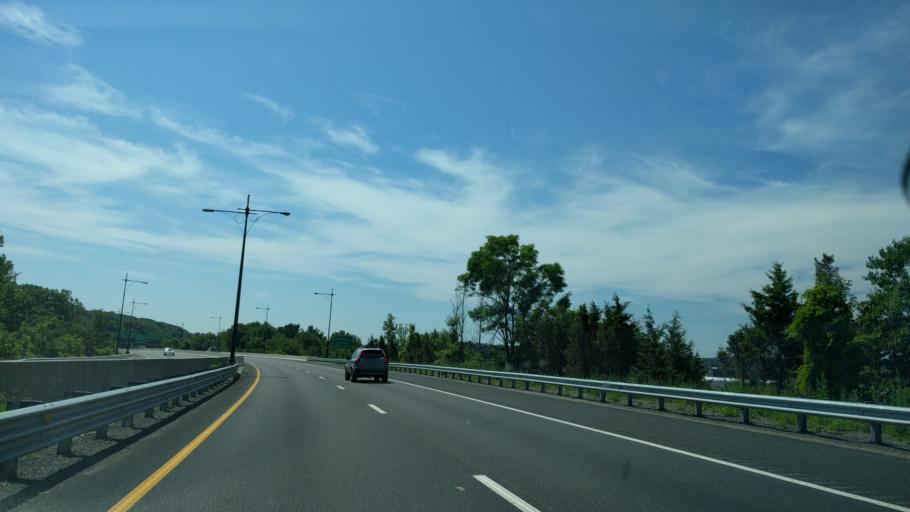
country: US
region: Massachusetts
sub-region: Worcester County
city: Sunderland
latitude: 42.2174
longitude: -71.7861
